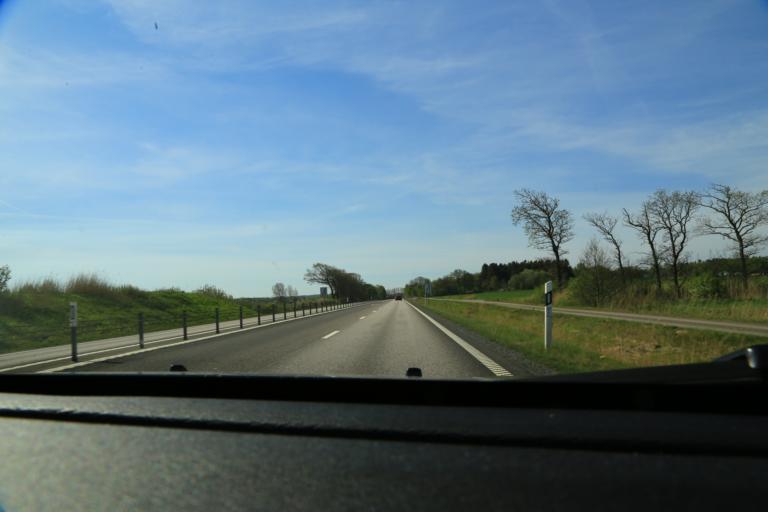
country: SE
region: Halland
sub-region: Varbergs Kommun
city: Varberg
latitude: 57.1588
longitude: 12.2715
